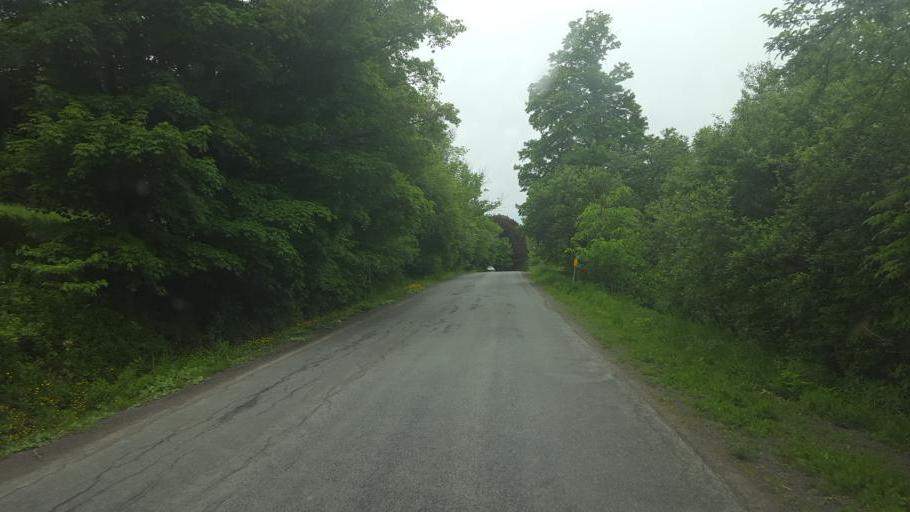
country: US
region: New York
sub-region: Oneida County
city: Waterville
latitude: 42.8536
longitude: -75.2204
